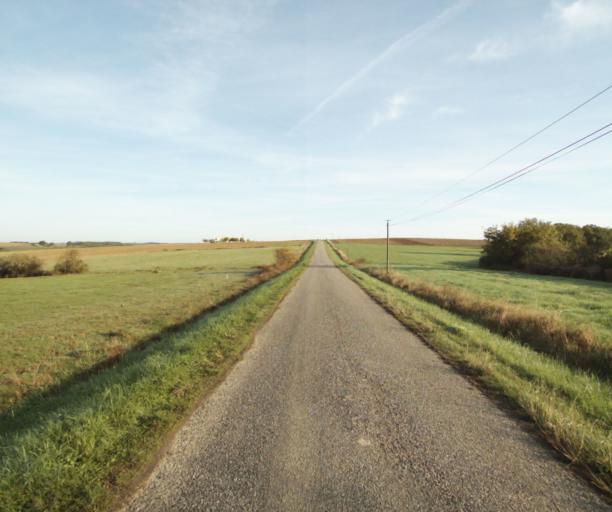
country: FR
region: Midi-Pyrenees
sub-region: Departement du Tarn-et-Garonne
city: Nohic
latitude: 43.9161
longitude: 1.4804
